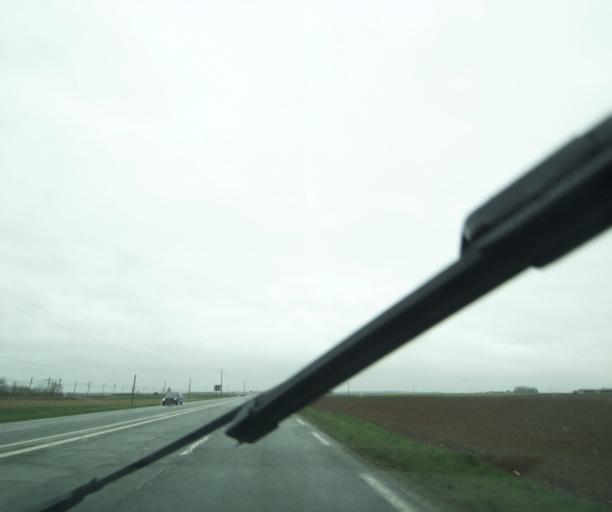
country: FR
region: Centre
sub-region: Departement du Loiret
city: Artenay
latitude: 48.0678
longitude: 1.8774
